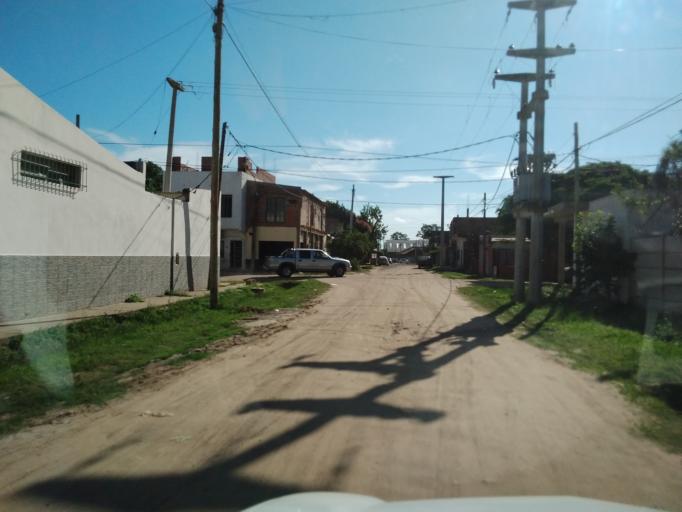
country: AR
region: Corrientes
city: Corrientes
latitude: -27.4844
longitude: -58.8140
